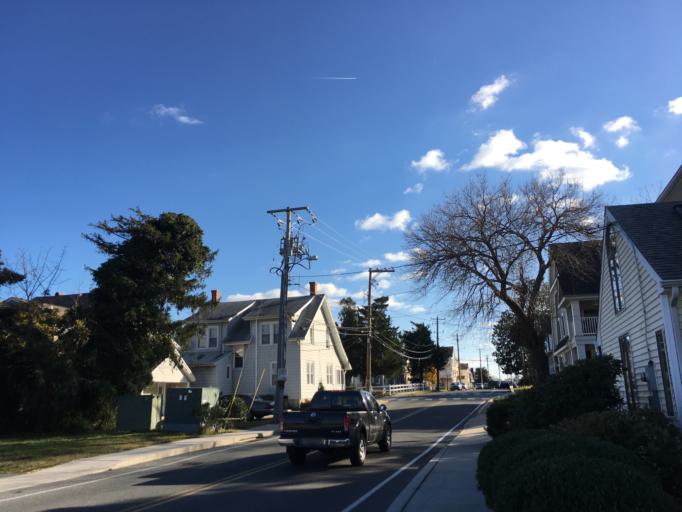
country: US
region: Delaware
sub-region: Sussex County
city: Rehoboth Beach
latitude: 38.7200
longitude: -75.0799
